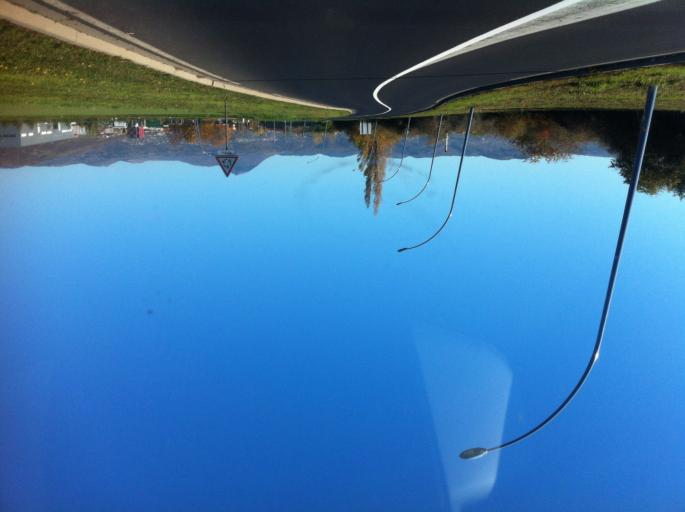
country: FR
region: Auvergne
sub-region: Departement du Puy-de-Dome
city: Aulnat
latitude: 45.7977
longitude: 3.1605
